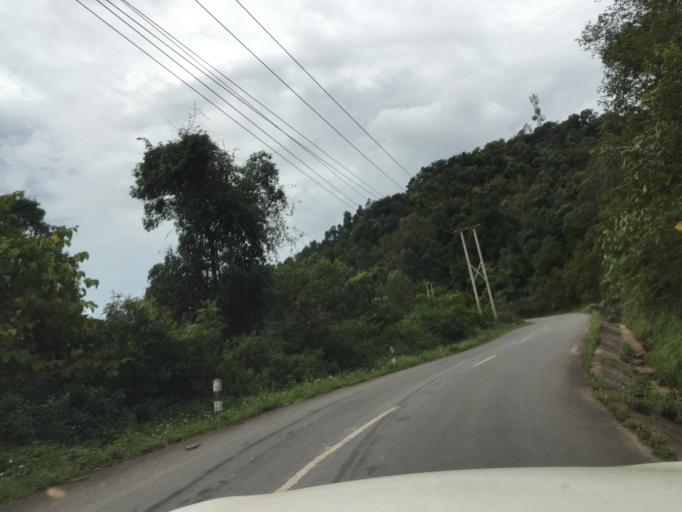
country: LA
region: Phongsali
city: Phongsali
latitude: 21.3092
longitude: 102.0491
